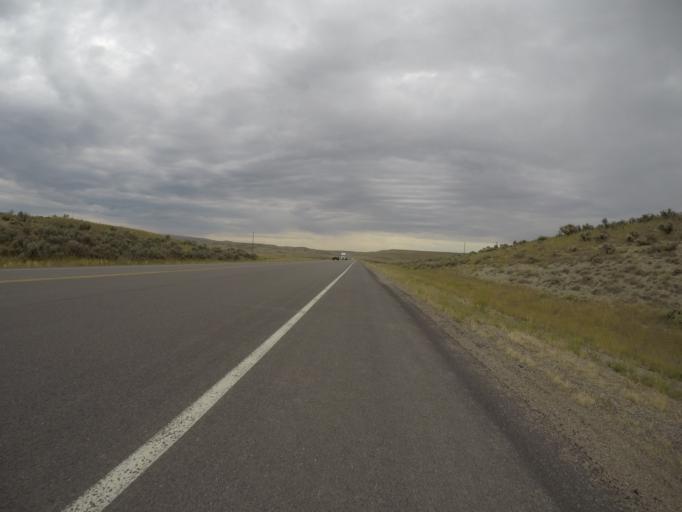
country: US
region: Wyoming
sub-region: Lincoln County
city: Kemmerer
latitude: 41.8018
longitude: -110.5999
